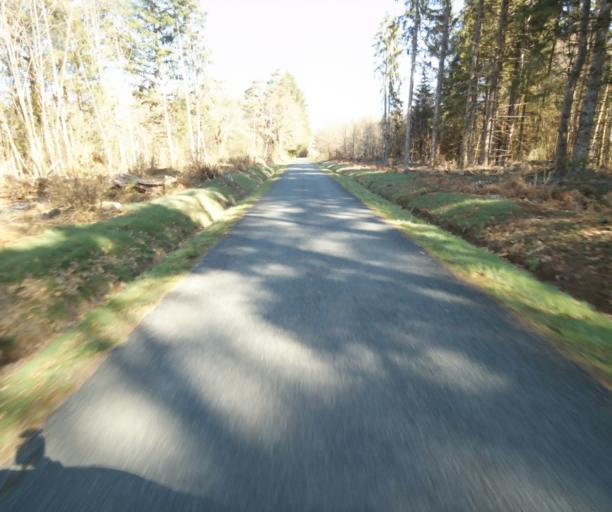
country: FR
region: Limousin
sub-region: Departement de la Correze
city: Correze
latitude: 45.2744
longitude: 1.9241
